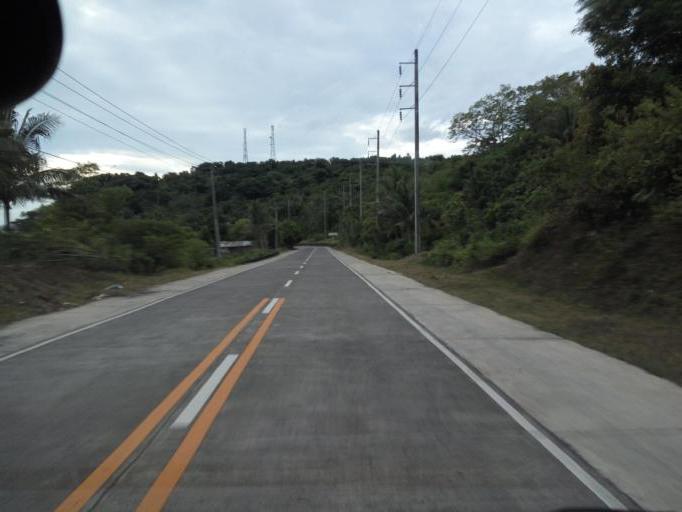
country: PH
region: Cagayan Valley
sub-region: Province of Cagayan
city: Casambalangan
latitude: 18.3952
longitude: 122.1330
